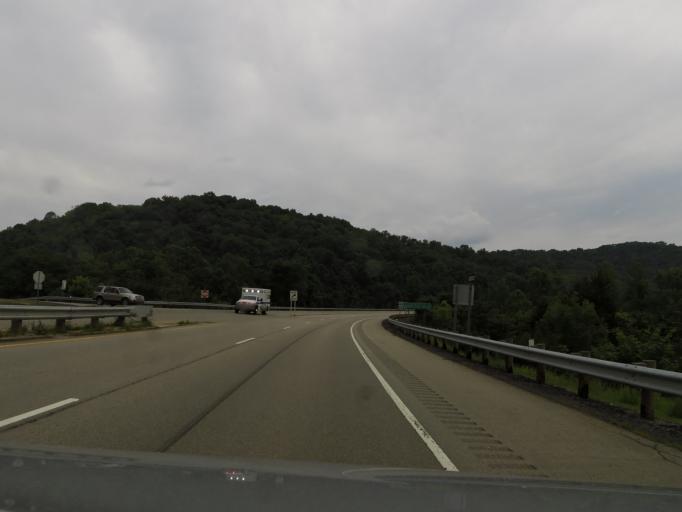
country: US
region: Ohio
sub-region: Brown County
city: Ripley
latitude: 38.7539
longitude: -83.8260
